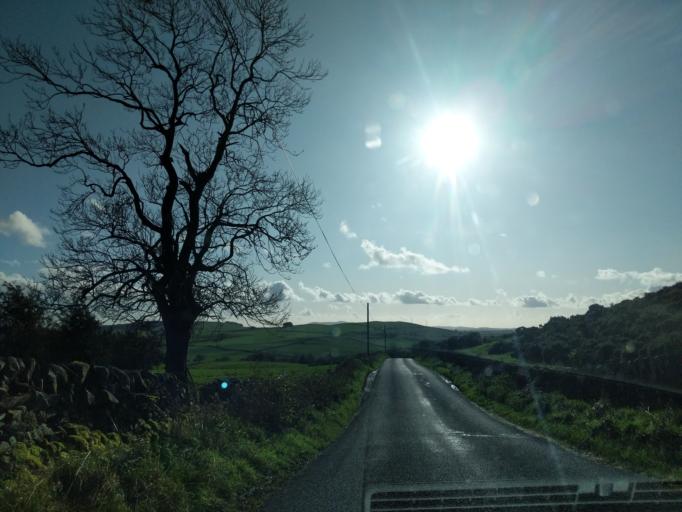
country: GB
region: Scotland
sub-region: Dumfries and Galloway
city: Dalbeattie
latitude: 55.0361
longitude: -3.7624
